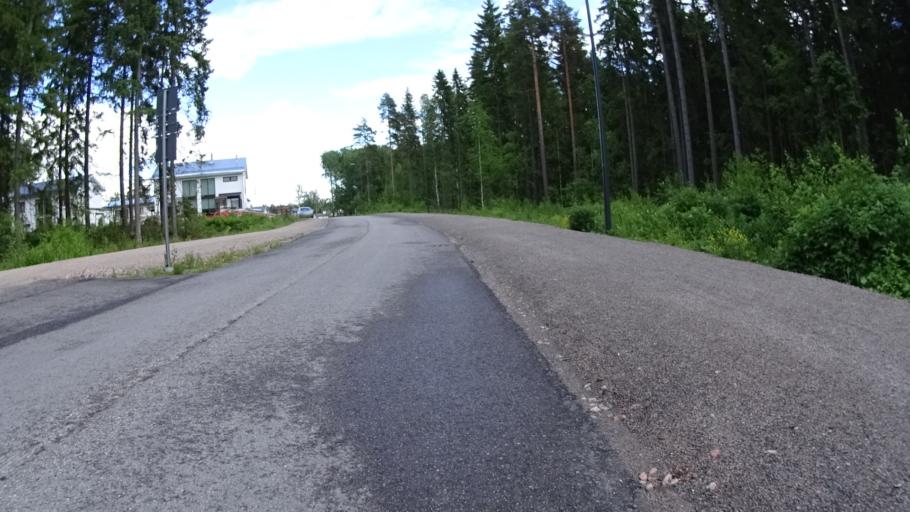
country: FI
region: Uusimaa
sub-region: Helsinki
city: Kilo
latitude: 60.2437
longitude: 24.8266
